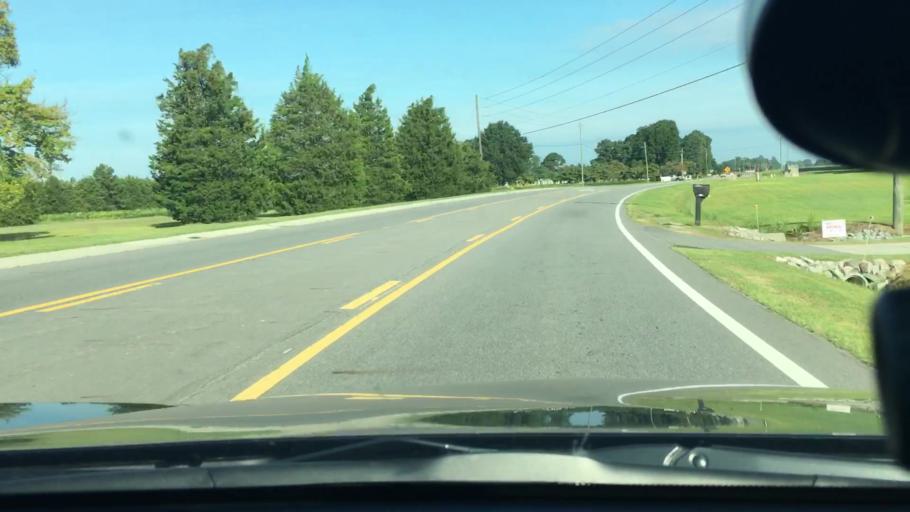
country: US
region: North Carolina
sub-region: Pitt County
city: Summerfield
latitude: 35.6462
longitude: -77.4602
